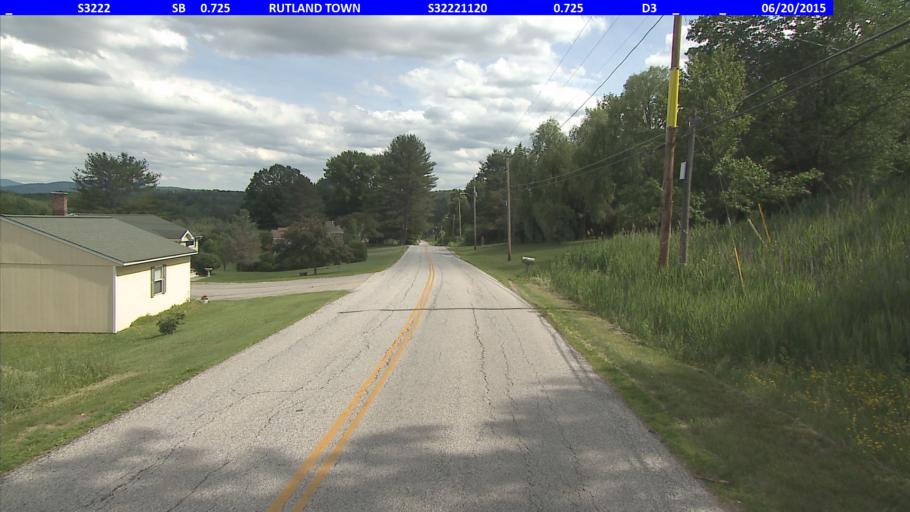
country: US
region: Vermont
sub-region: Rutland County
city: West Rutland
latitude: 43.6086
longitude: -73.0271
